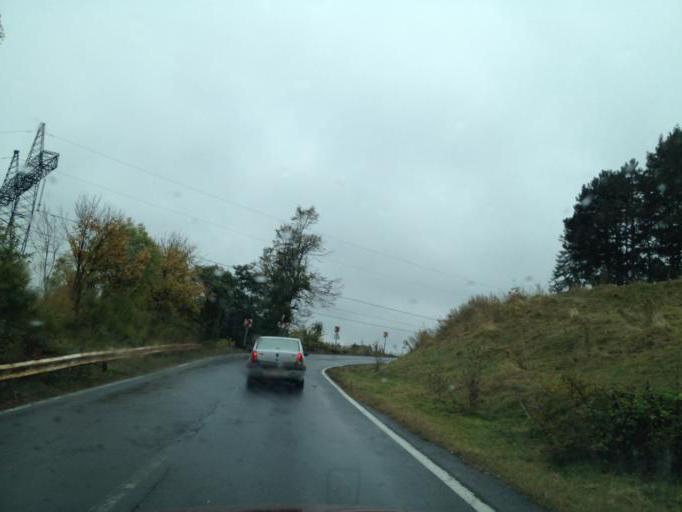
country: RO
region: Arges
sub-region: Comuna Dragoslavele
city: Dragoslavele
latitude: 45.3074
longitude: 25.1573
